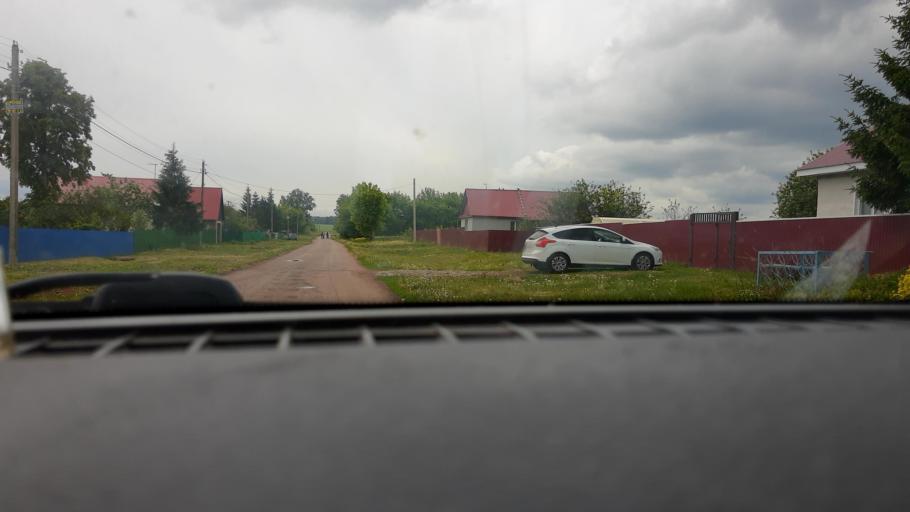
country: RU
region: Bashkortostan
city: Dmitriyevka
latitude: 54.7209
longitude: 55.4926
